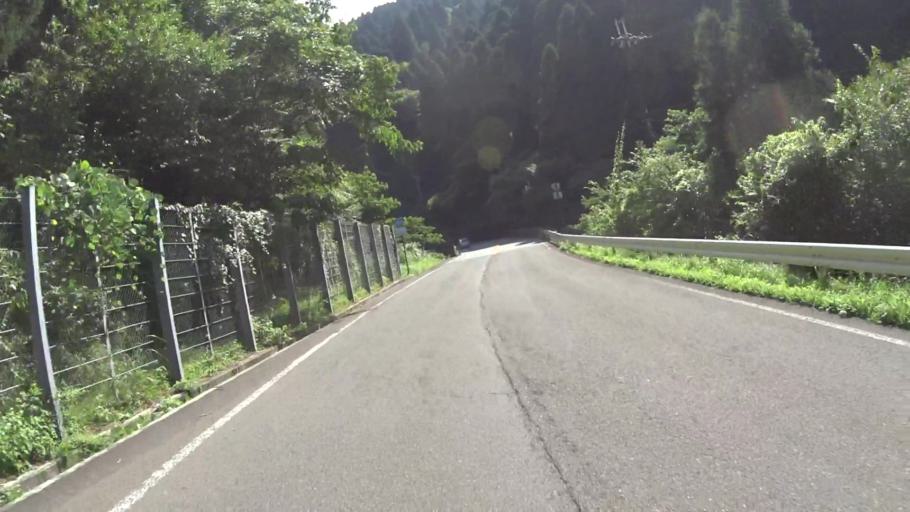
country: JP
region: Fukui
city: Obama
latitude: 35.3863
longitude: 135.5824
